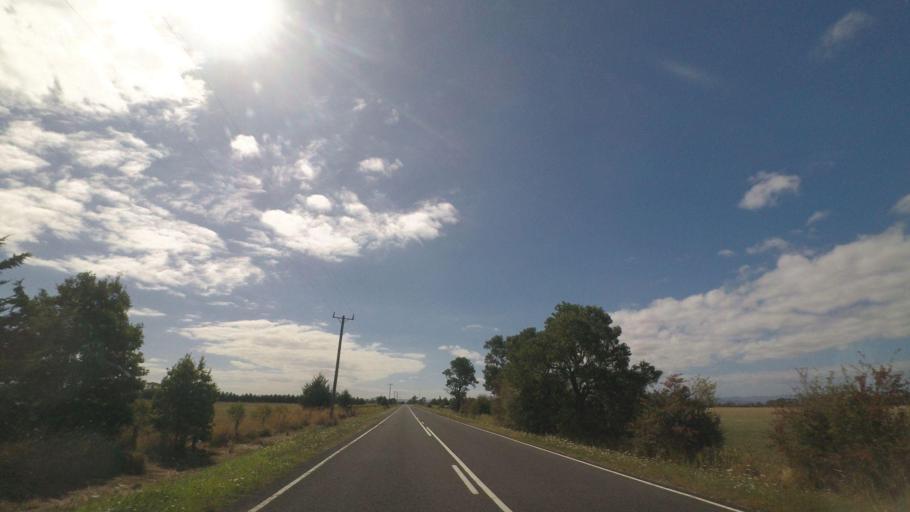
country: AU
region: Victoria
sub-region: Cardinia
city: Garfield
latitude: -38.2059
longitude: 145.6326
